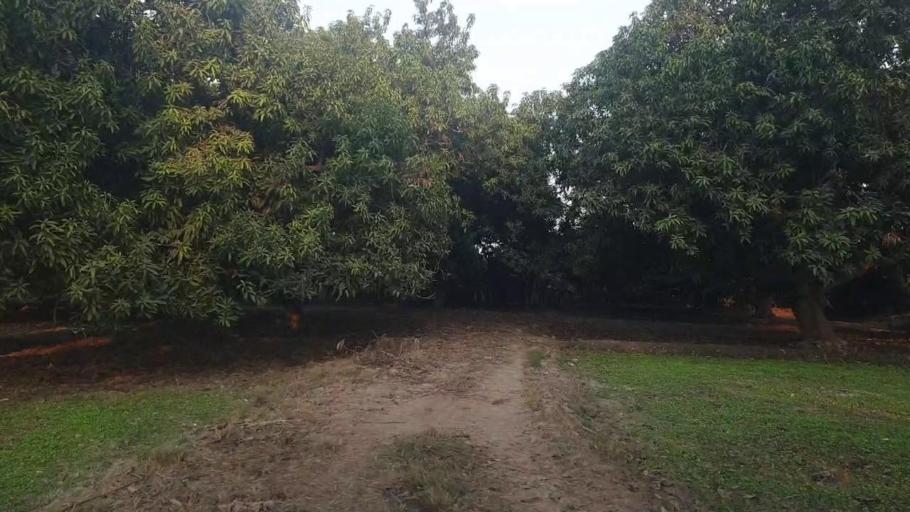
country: PK
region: Sindh
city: Tando Jam
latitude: 25.4412
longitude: 68.5940
